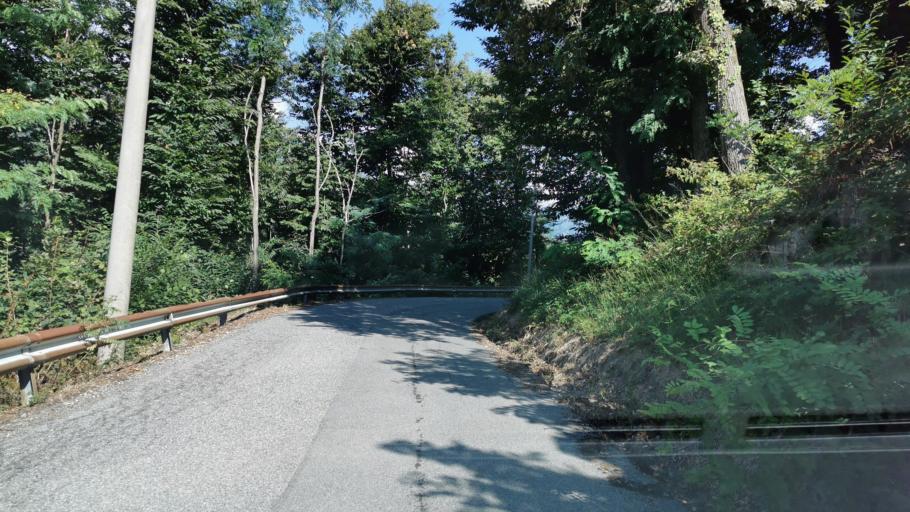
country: IT
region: Piedmont
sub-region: Provincia di Biella
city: Pollone
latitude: 45.5898
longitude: 8.0066
